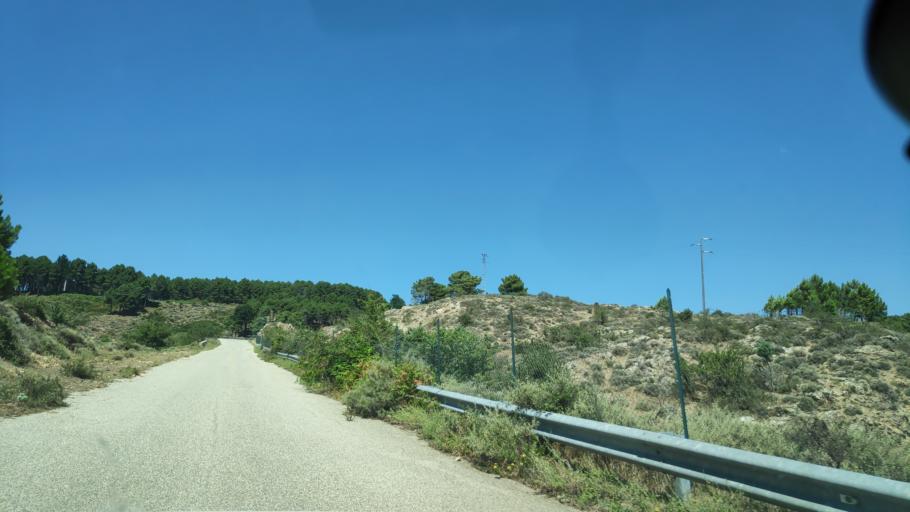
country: IT
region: Calabria
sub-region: Provincia di Reggio Calabria
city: Bova
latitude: 38.0236
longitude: 15.9401
